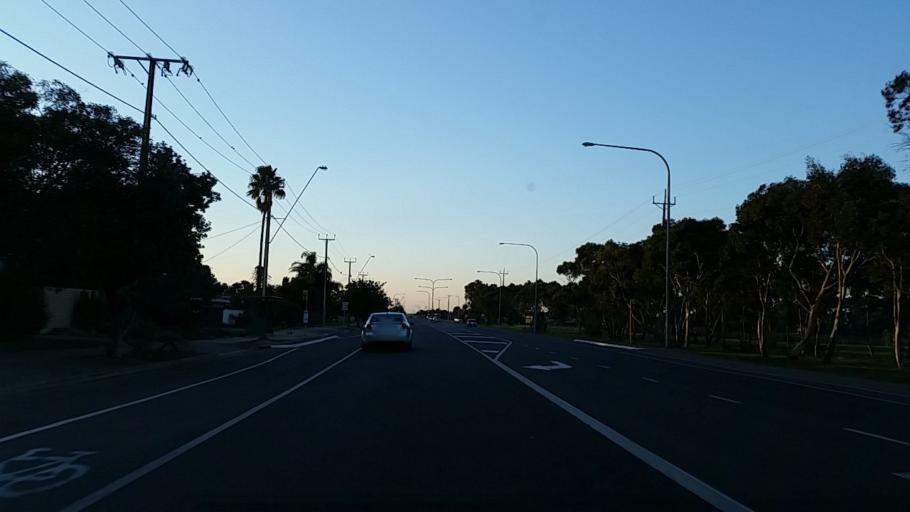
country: AU
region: South Australia
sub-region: Onkaparinga
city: Seaford
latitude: -35.1839
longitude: 138.4770
